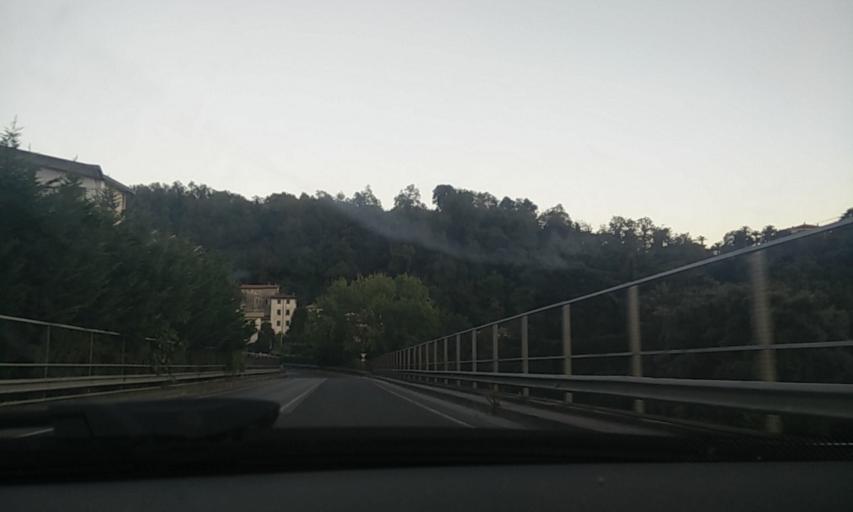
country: IT
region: Tuscany
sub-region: Provincia di Massa-Carrara
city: Carrara
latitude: 44.0695
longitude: 10.0855
